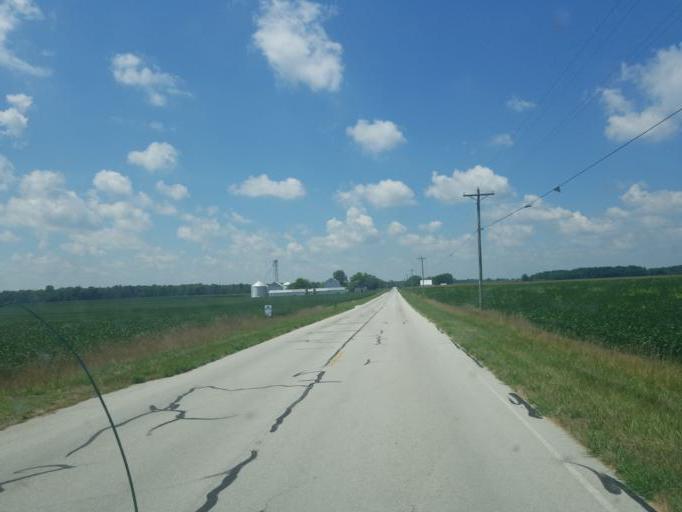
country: US
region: Ohio
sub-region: Allen County
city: Spencerville
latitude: 40.6771
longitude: -84.4887
